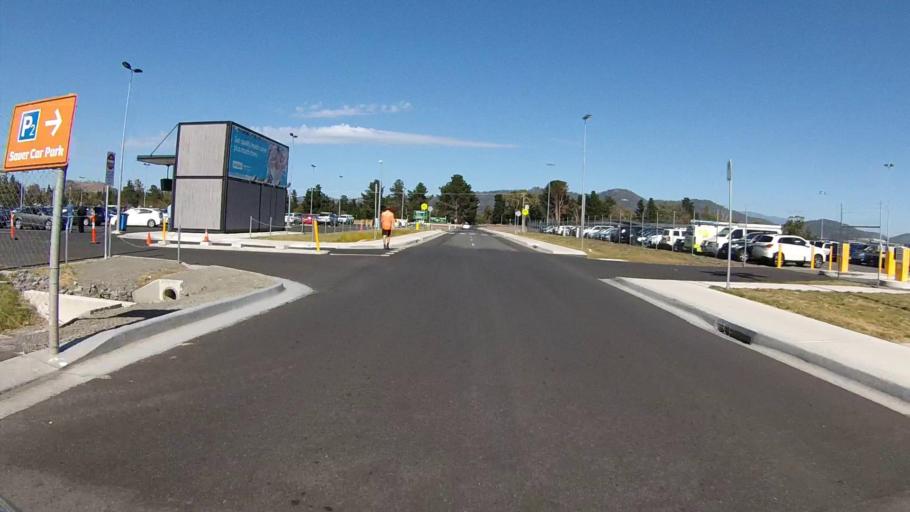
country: AU
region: Tasmania
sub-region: Clarence
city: Seven Mile Beach
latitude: -42.8400
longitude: 147.5047
